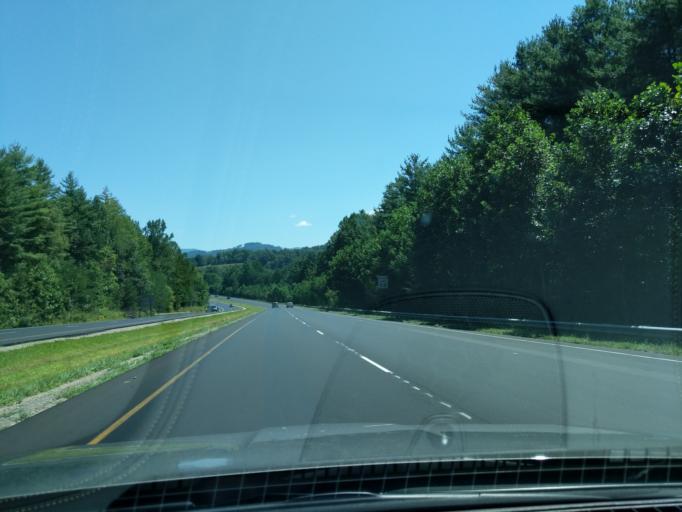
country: US
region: North Carolina
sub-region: Macon County
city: Franklin
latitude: 35.1648
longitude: -83.3822
